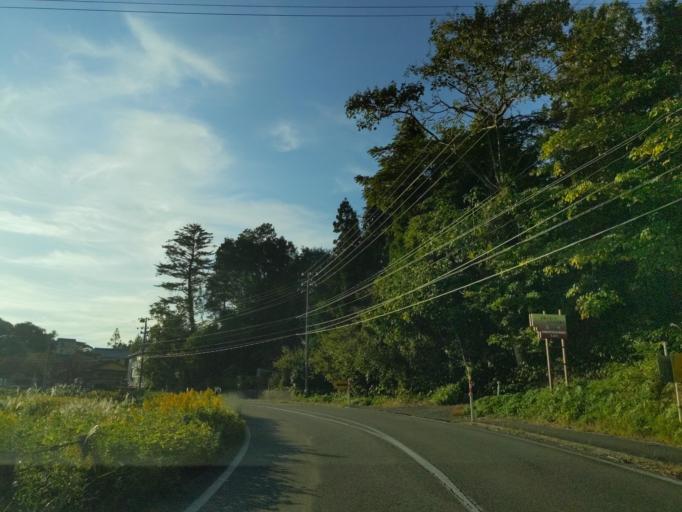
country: JP
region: Niigata
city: Nagaoka
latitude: 37.5792
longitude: 138.7633
